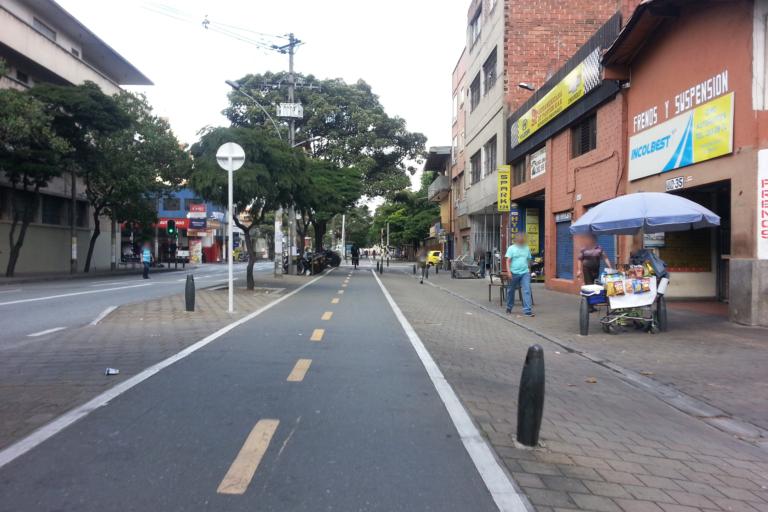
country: CO
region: Antioquia
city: Medellin
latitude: 6.2615
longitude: -75.5669
